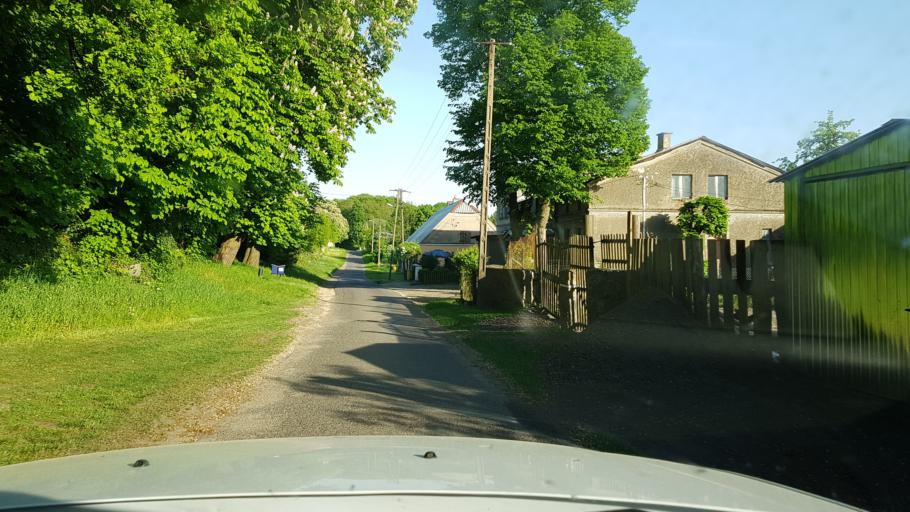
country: PL
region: West Pomeranian Voivodeship
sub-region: Powiat lobeski
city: Radowo Male
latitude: 53.6512
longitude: 15.3646
